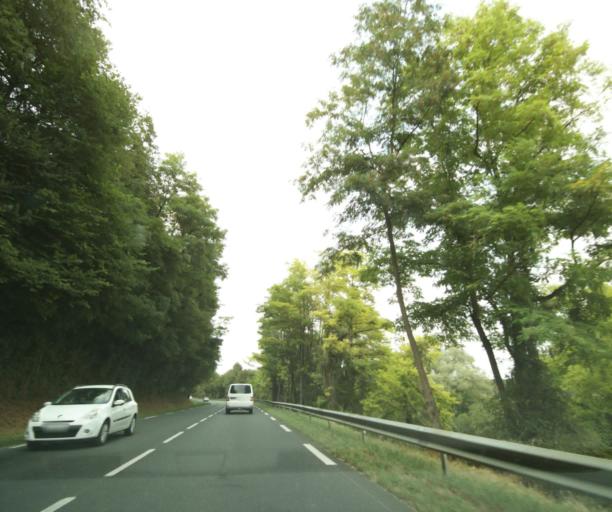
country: FR
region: Centre
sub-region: Departement de l'Indre
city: Clion
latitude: 46.9552
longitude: 1.2159
